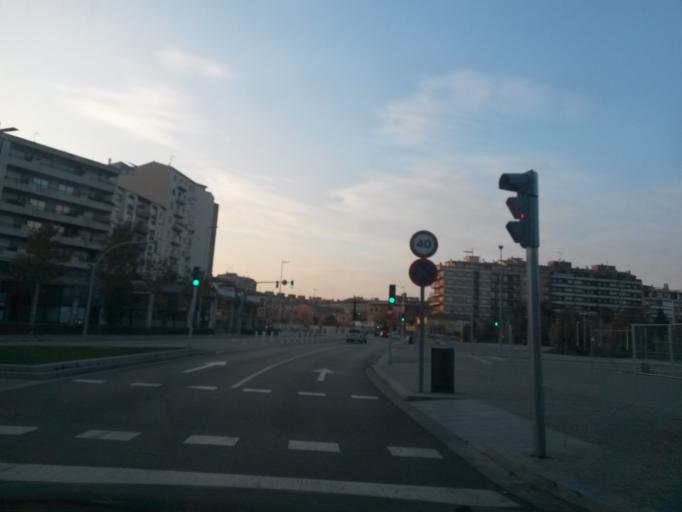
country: ES
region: Catalonia
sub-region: Provincia de Girona
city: Girona
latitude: 41.9761
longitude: 2.8152
